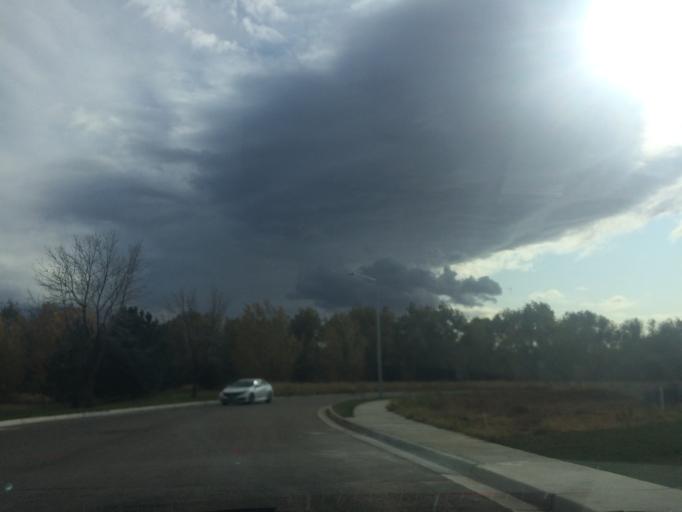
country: US
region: Colorado
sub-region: Boulder County
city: Longmont
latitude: 40.1365
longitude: -105.1248
